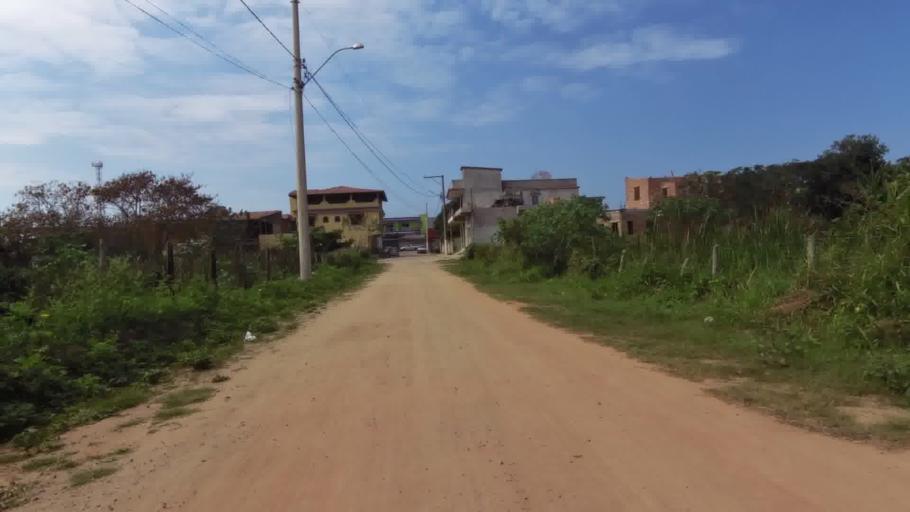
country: BR
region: Espirito Santo
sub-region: Marataizes
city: Marataizes
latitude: -21.0253
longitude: -40.8178
